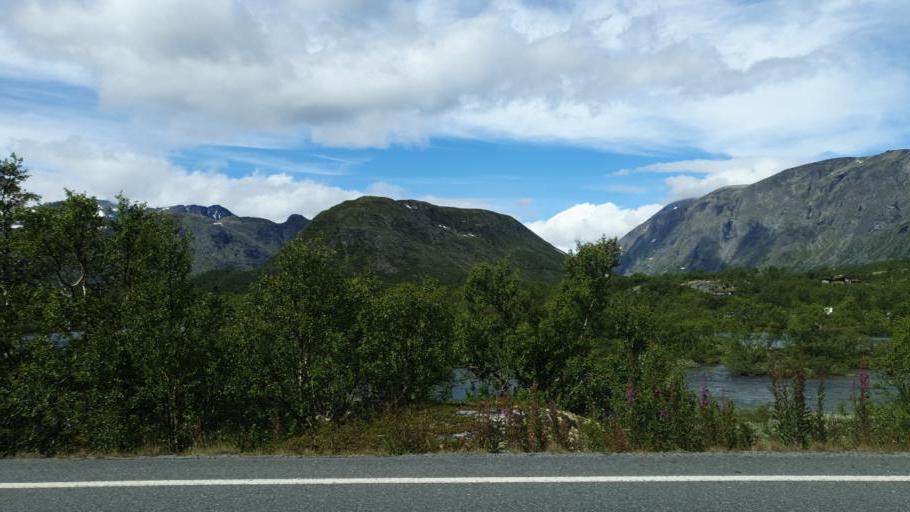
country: NO
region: Oppland
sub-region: Oystre Slidre
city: Heggenes
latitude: 61.4863
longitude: 8.8378
